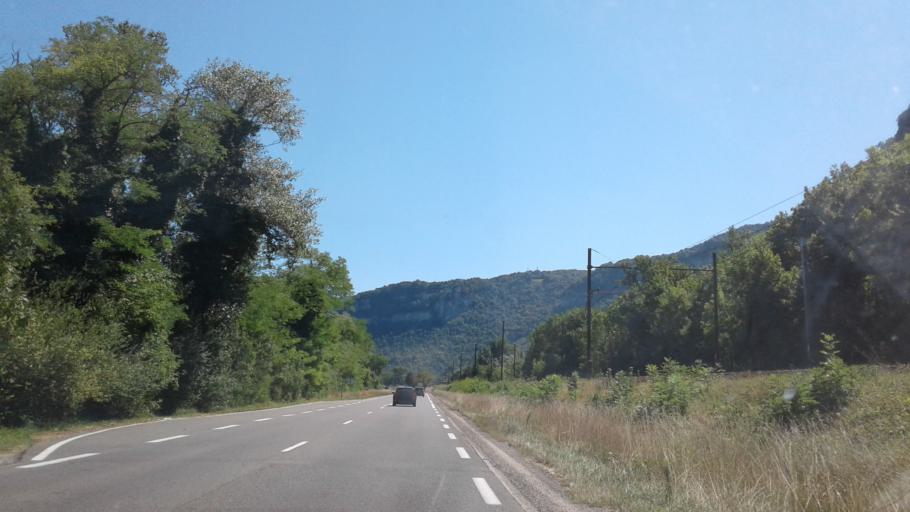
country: FR
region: Rhone-Alpes
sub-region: Departement de l'Ain
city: Vaux-en-Bugey
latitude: 45.9306
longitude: 5.3846
